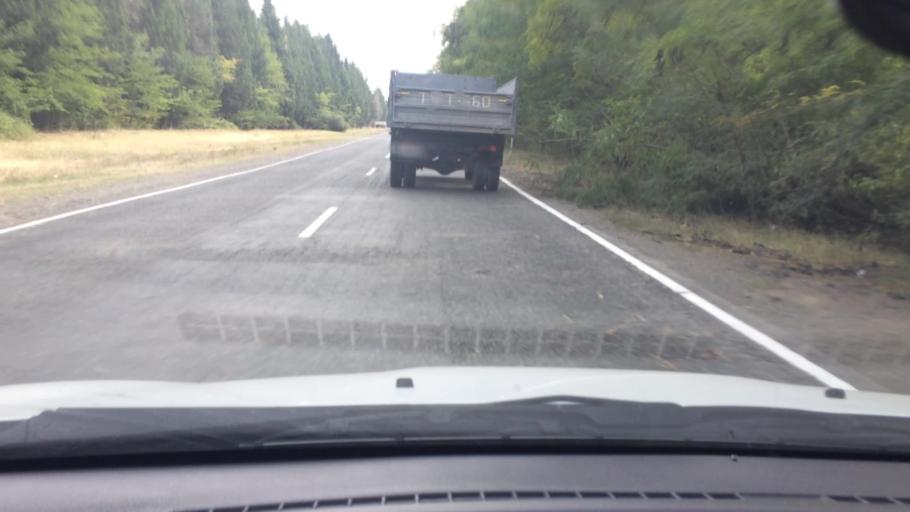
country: GE
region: Kvemo Kartli
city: Rust'avi
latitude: 41.4676
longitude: 44.9814
